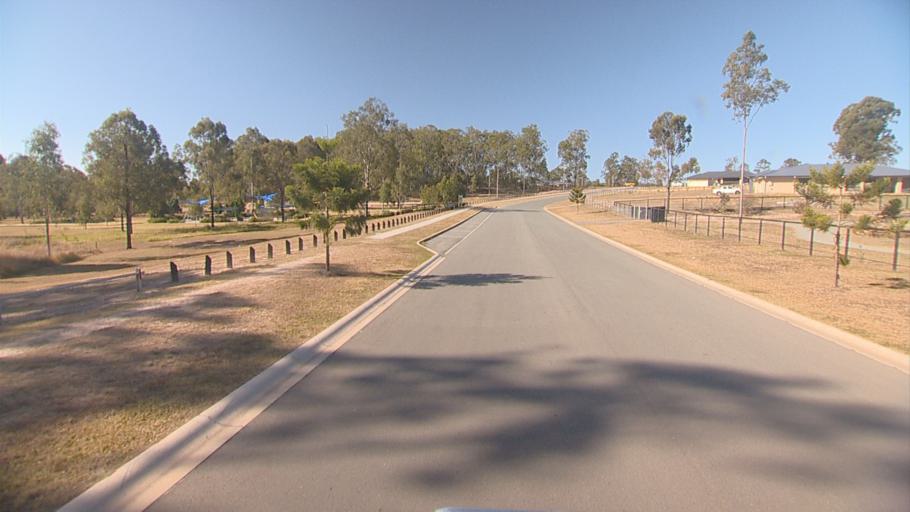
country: AU
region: Queensland
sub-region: Logan
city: Cedar Vale
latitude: -27.8668
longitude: 153.0508
